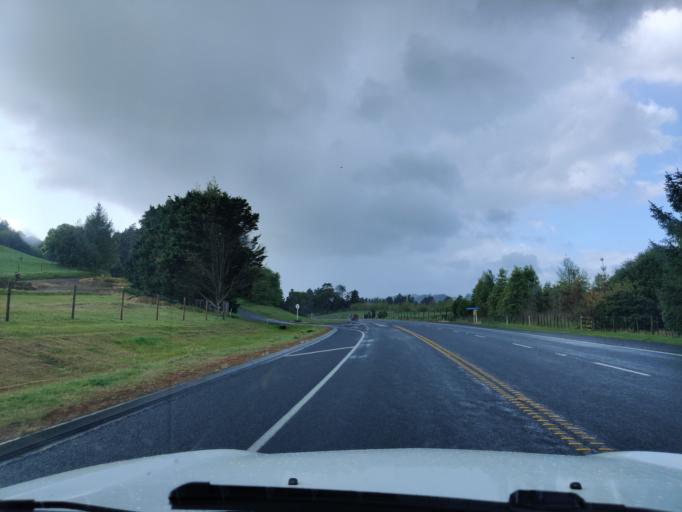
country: NZ
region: Waikato
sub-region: Waipa District
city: Cambridge
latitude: -37.9387
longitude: 175.5768
